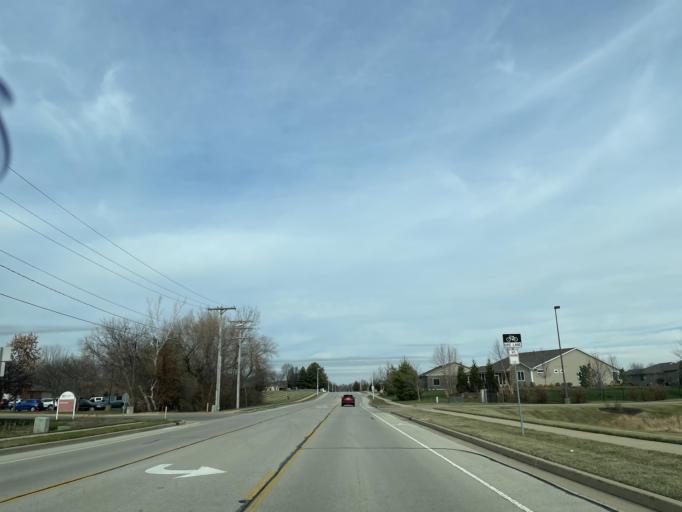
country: US
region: Illinois
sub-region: Sangamon County
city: Jerome
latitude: 39.7721
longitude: -89.7298
